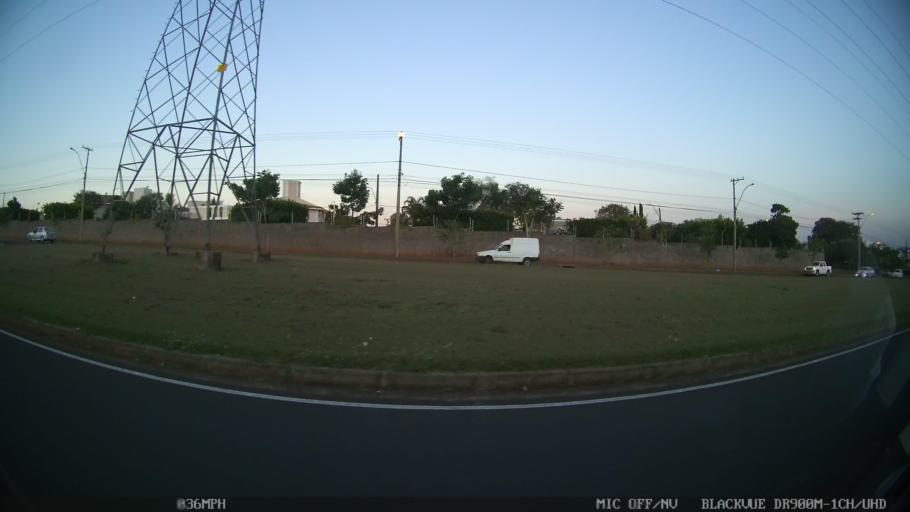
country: BR
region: Sao Paulo
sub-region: Sao Jose Do Rio Preto
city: Sao Jose do Rio Preto
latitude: -20.8193
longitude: -49.3396
